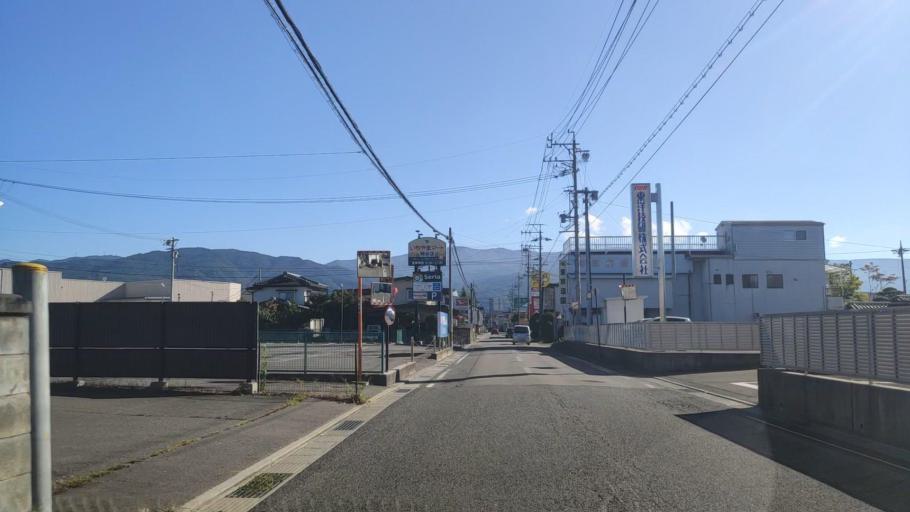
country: JP
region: Nagano
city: Okaya
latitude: 36.0629
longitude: 138.0715
